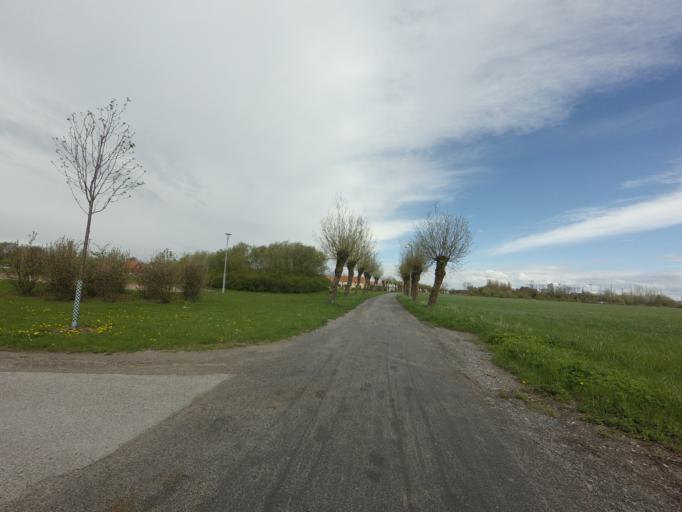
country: SE
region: Skane
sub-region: Malmo
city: Bunkeflostrand
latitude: 55.5520
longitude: 12.9664
